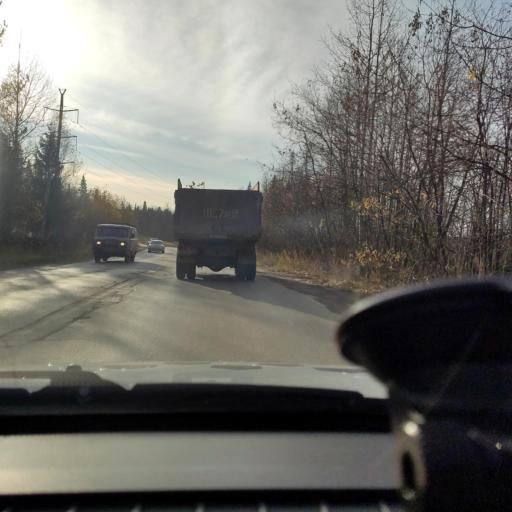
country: RU
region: Perm
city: Ferma
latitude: 57.9627
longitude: 56.3547
